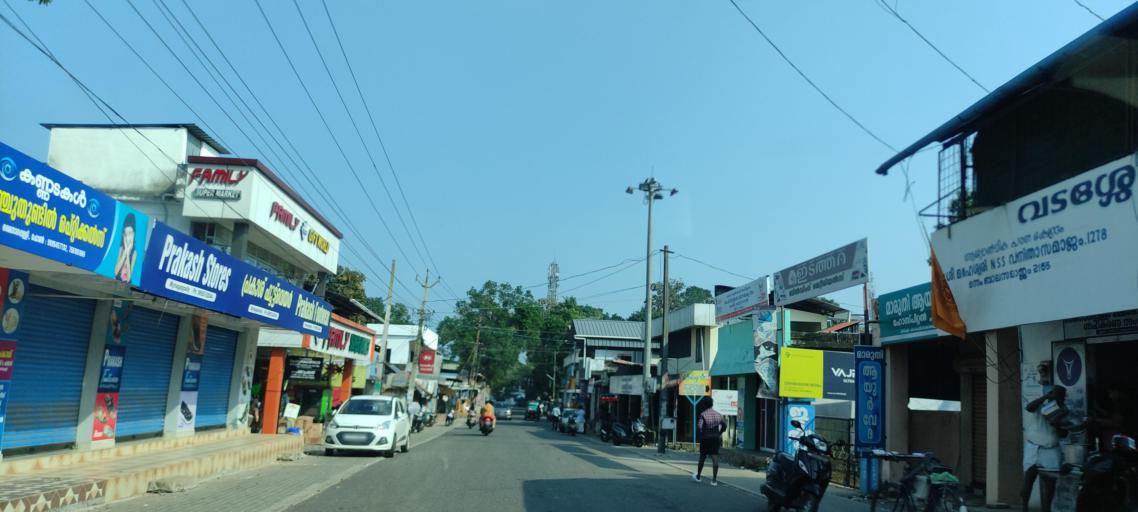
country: IN
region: Kerala
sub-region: Kollam
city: Panmana
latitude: 9.0427
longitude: 76.5826
